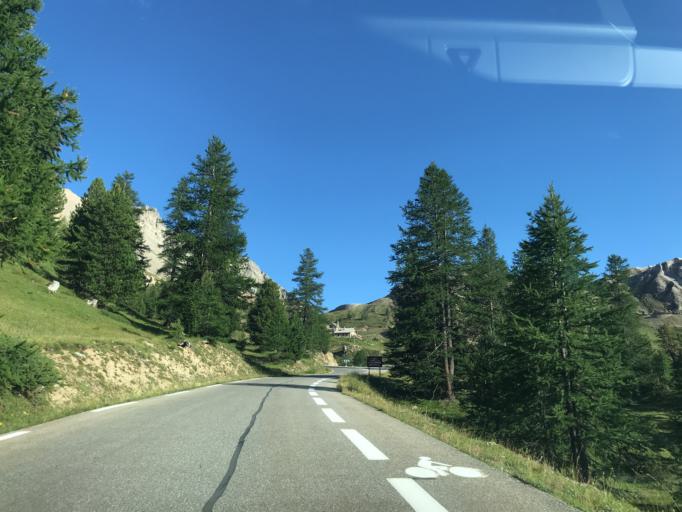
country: FR
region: Provence-Alpes-Cote d'Azur
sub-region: Departement des Hautes-Alpes
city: Villar-Saint-Pancrace
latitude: 44.8259
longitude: 6.7307
